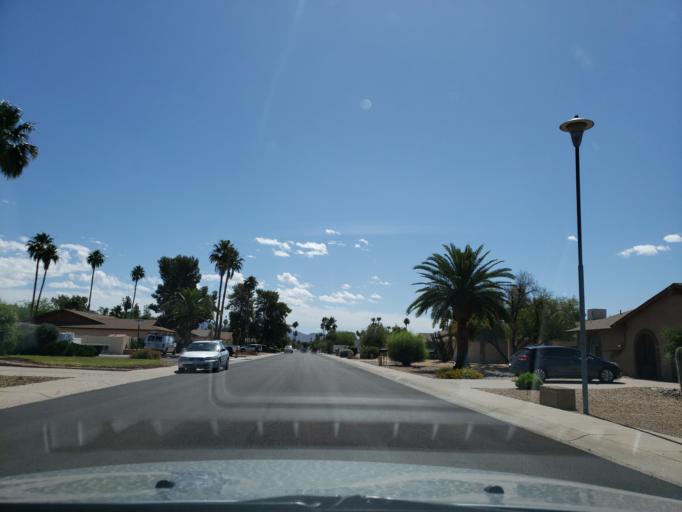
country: US
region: Arizona
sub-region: Maricopa County
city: Paradise Valley
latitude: 33.6150
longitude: -111.9542
